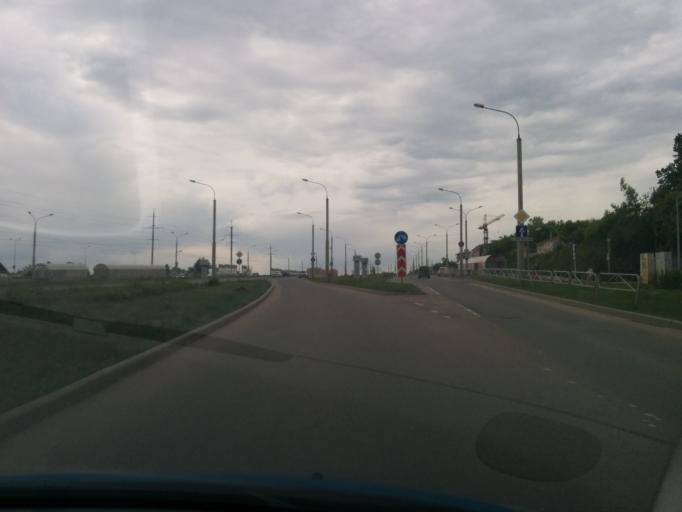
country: RU
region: Perm
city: Perm
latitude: 57.9990
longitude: 56.3114
